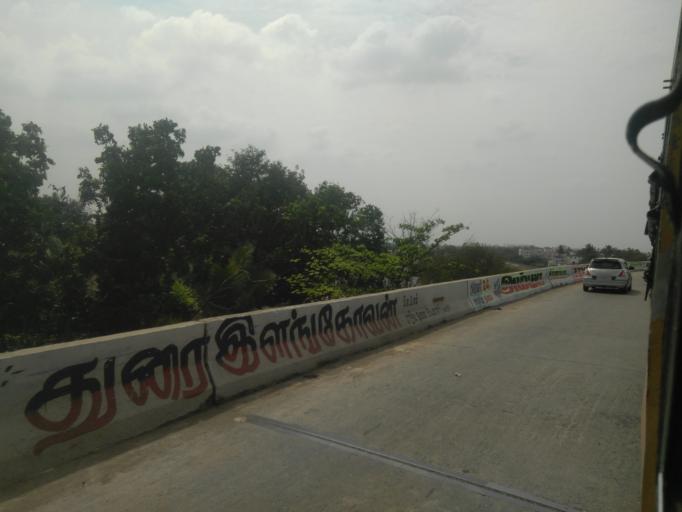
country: IN
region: Tamil Nadu
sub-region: Coimbatore
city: Irugur
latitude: 11.0020
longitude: 77.0555
